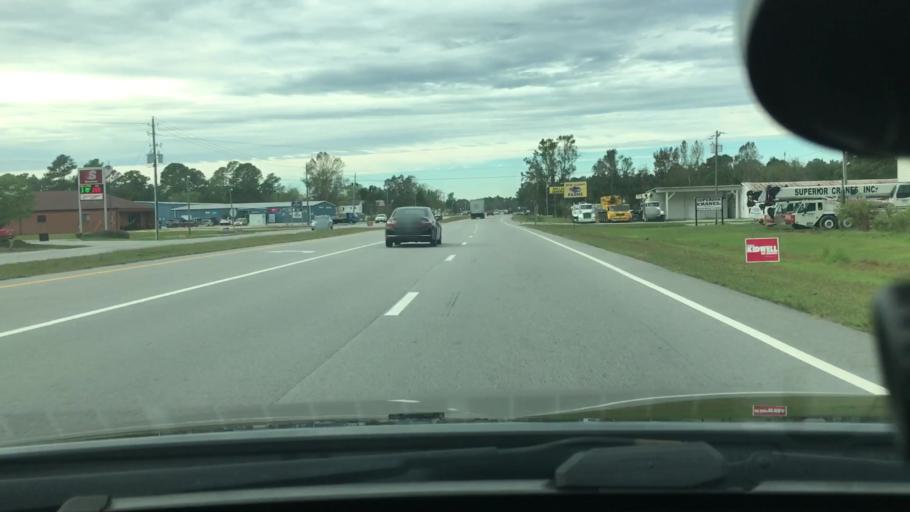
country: US
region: North Carolina
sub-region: Craven County
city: New Bern
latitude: 35.1218
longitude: -77.0188
